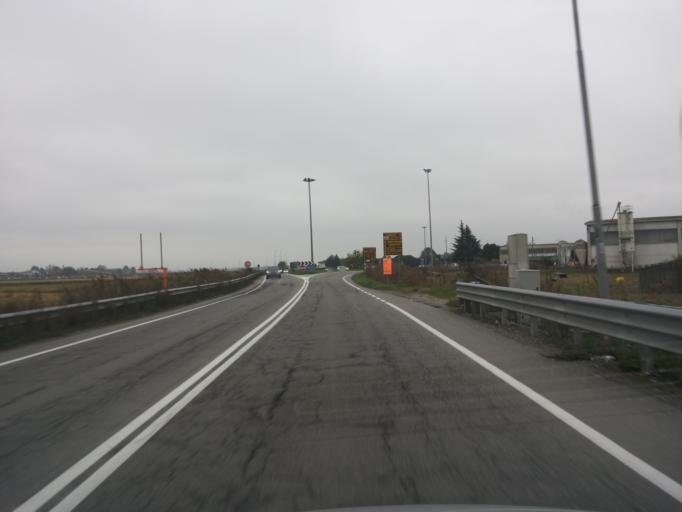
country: IT
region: Piedmont
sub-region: Provincia di Novara
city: Lumellogno
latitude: 45.4210
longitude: 8.5721
